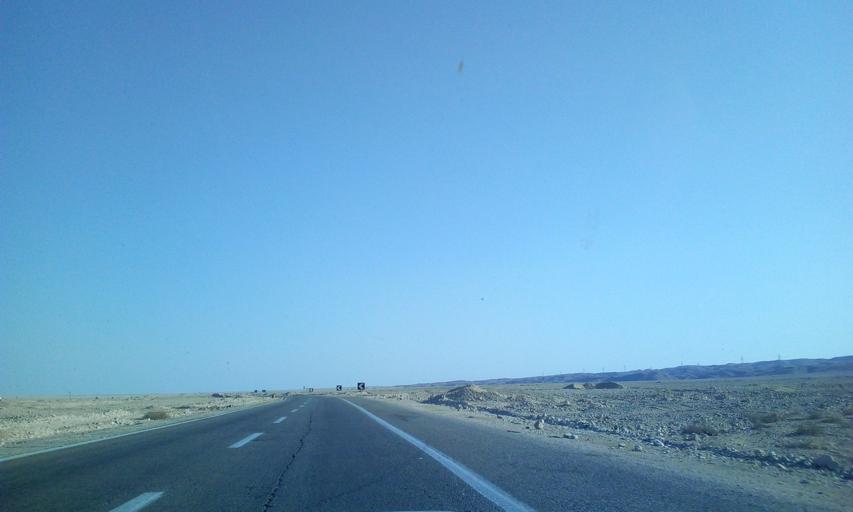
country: EG
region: As Suways
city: Ain Sukhna
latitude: 28.9655
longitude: 32.6191
